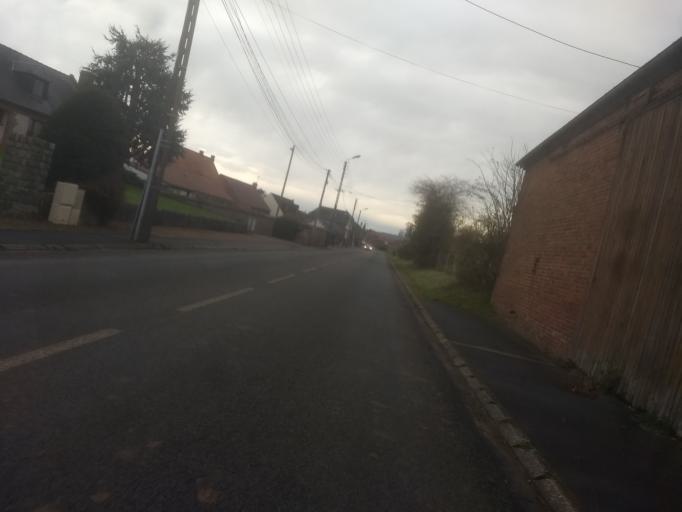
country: FR
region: Nord-Pas-de-Calais
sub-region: Departement du Pas-de-Calais
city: Riviere
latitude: 50.2354
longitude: 2.7006
